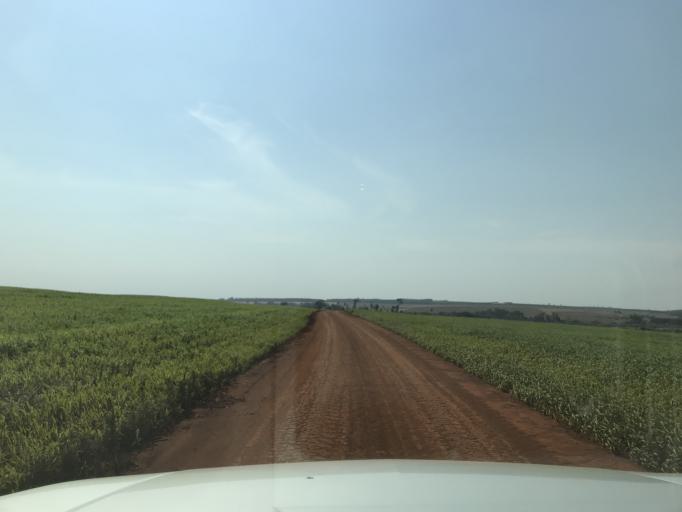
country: BR
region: Parana
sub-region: Palotina
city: Palotina
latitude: -24.2297
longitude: -53.7405
